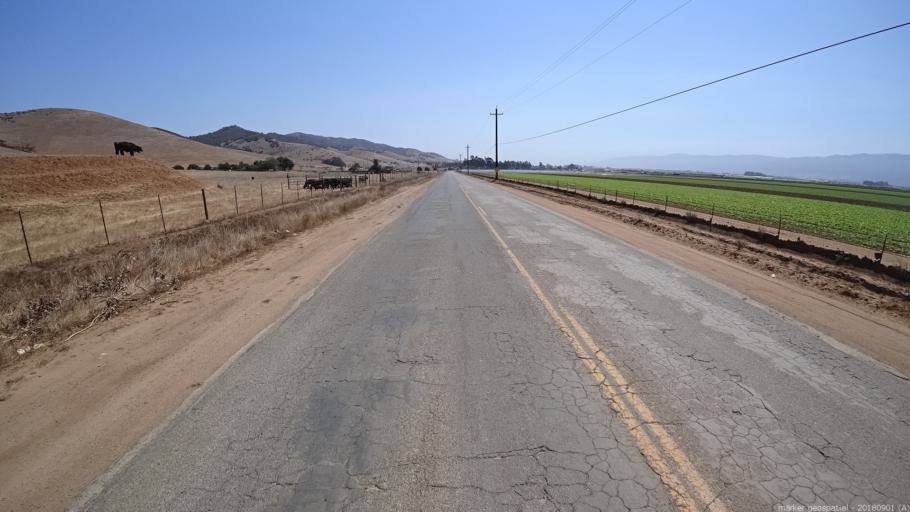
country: US
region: California
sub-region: Monterey County
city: Salinas
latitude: 36.6839
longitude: -121.5611
